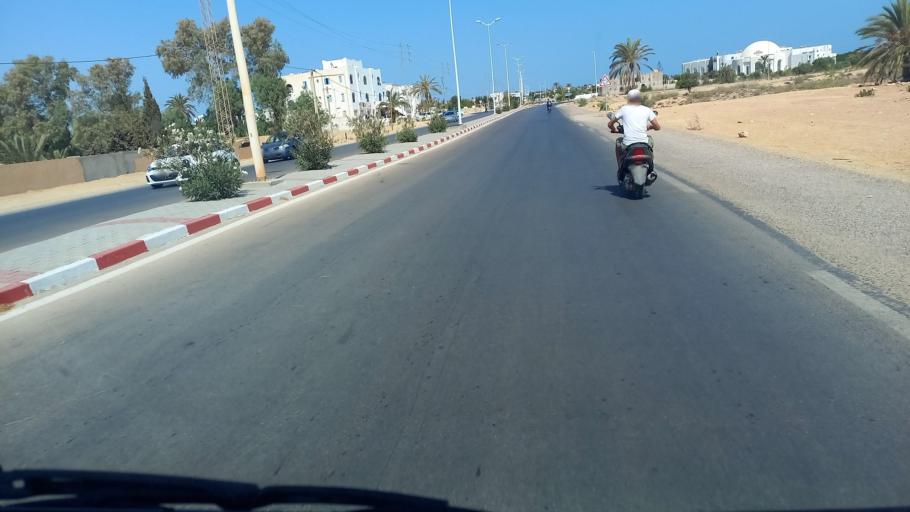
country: TN
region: Madanin
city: Midoun
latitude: 33.8551
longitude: 10.9786
